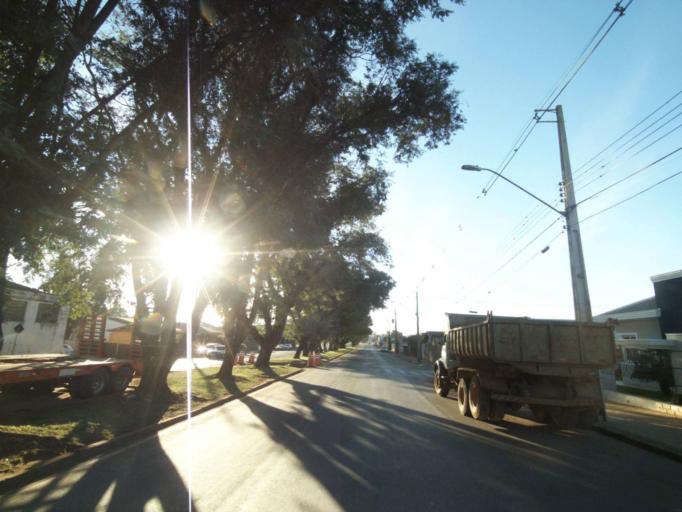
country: BR
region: Parana
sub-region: Tibagi
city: Tibagi
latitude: -24.5176
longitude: -50.4135
